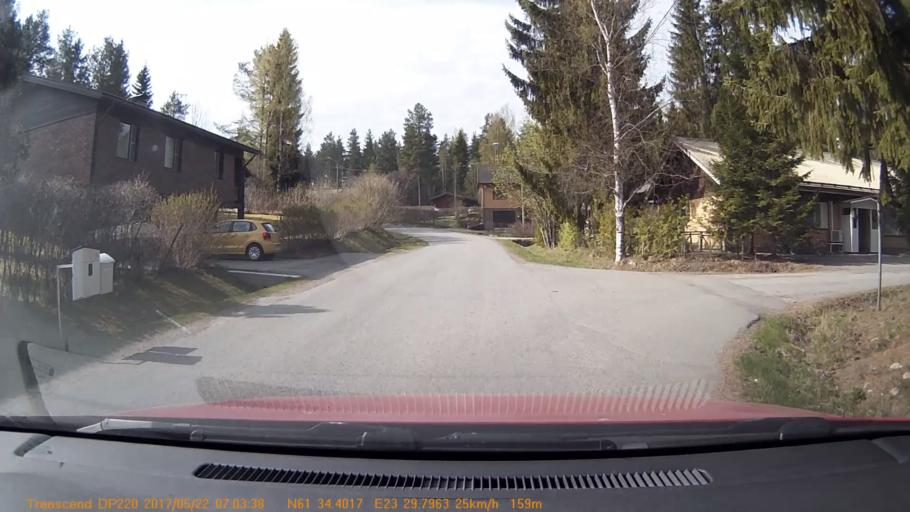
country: FI
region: Pirkanmaa
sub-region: Tampere
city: Yloejaervi
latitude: 61.5734
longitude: 23.4966
